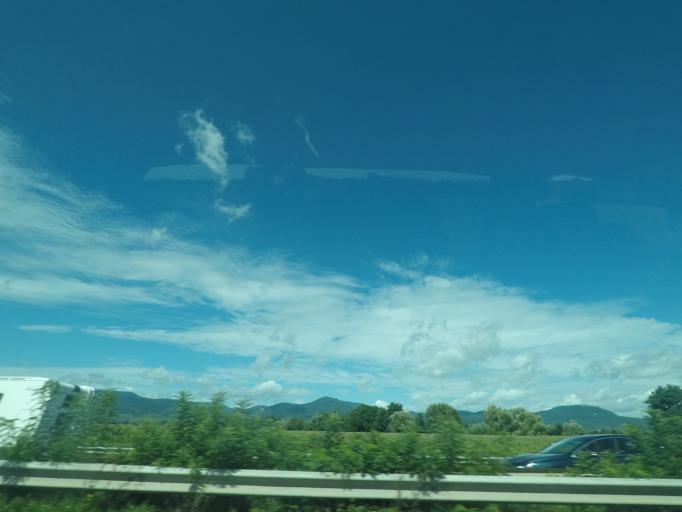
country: FR
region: Alsace
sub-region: Departement du Haut-Rhin
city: Guemar
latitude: 48.1789
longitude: 7.3827
